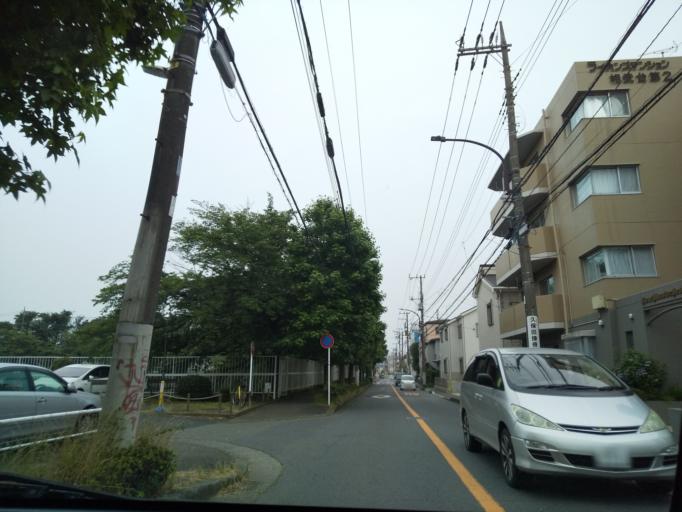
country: JP
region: Kanagawa
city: Zama
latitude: 35.5072
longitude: 139.4033
